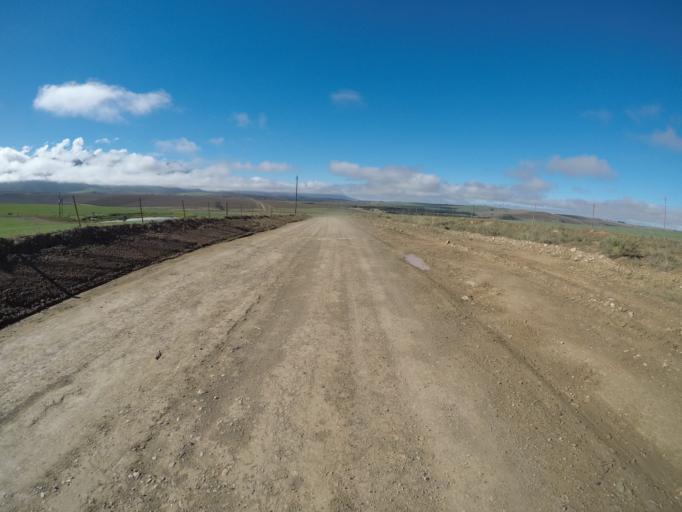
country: ZA
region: Western Cape
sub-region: Overberg District Municipality
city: Caledon
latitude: -34.1206
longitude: 19.7242
